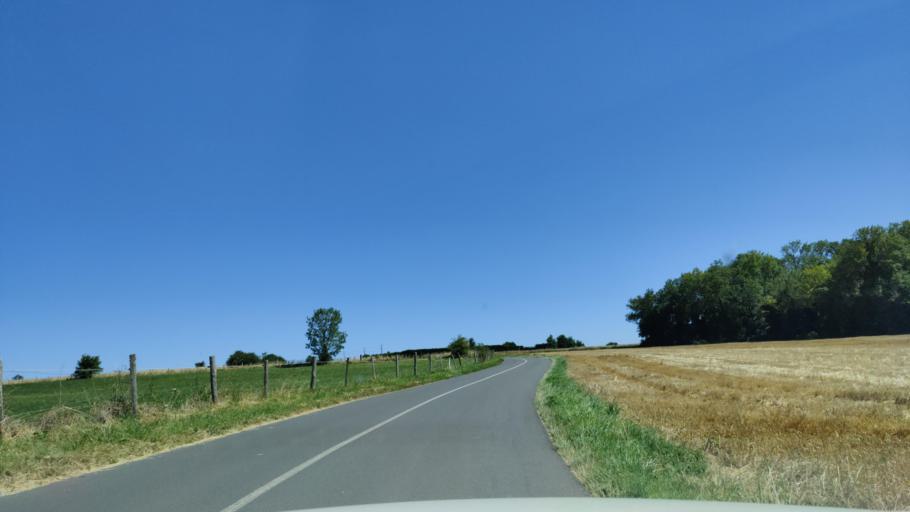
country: FR
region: Ile-de-France
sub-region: Departement de l'Essonne
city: Fontenay-les-Briis
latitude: 48.5977
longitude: 2.1639
